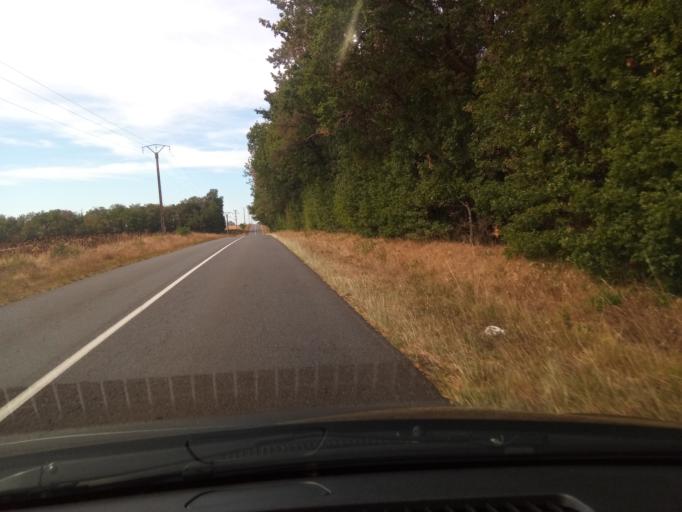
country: FR
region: Poitou-Charentes
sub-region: Departement de la Vienne
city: Chauvigny
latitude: 46.5217
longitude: 0.7429
